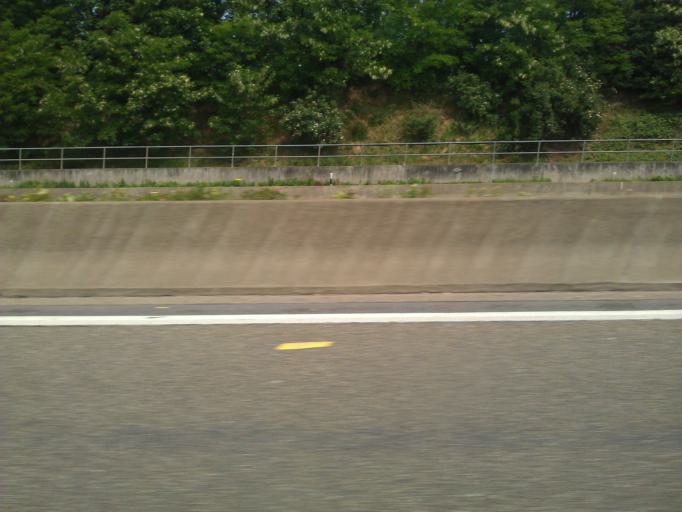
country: DE
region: North Rhine-Westphalia
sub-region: Regierungsbezirk Koln
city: Frechen
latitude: 50.9229
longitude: 6.8544
